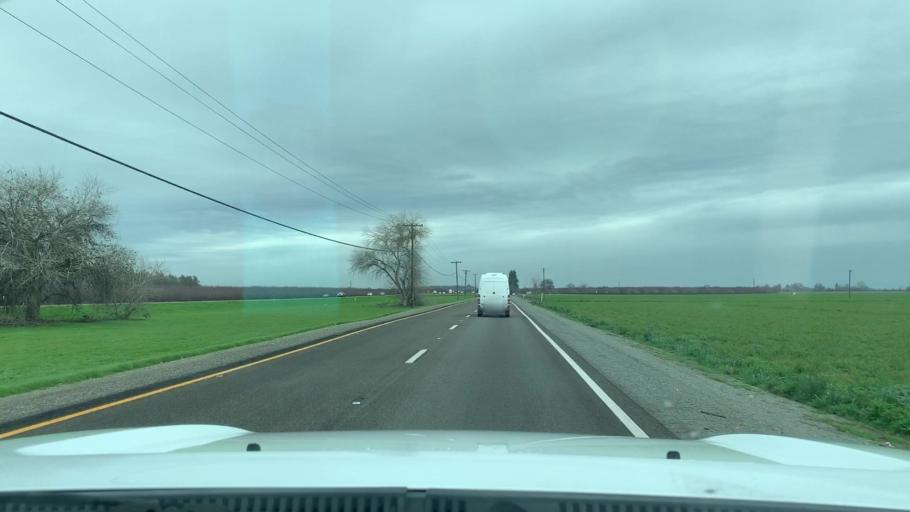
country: US
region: California
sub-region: Fresno County
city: Riverdale
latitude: 36.3751
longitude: -119.8096
